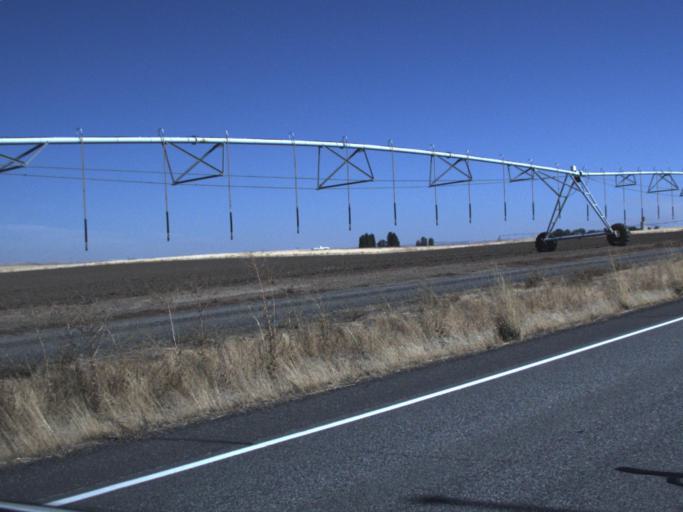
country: US
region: Washington
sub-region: Walla Walla County
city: Garrett
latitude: 46.2967
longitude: -118.6515
